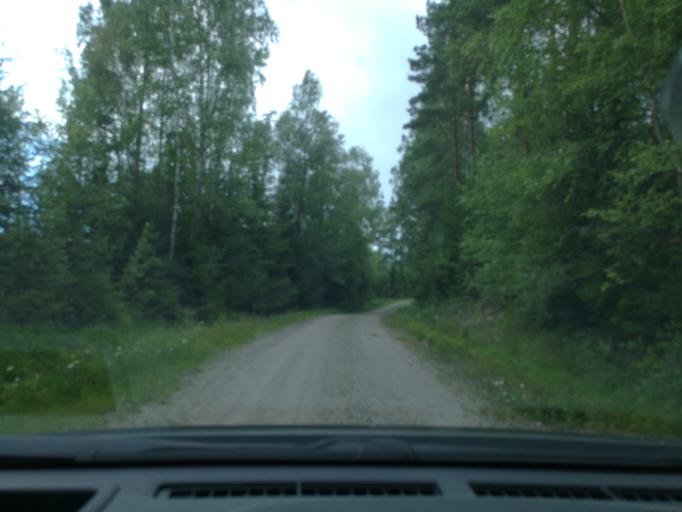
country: SE
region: Vaestmanland
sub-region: Surahammars Kommun
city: Ramnas
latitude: 59.8126
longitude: 16.2775
